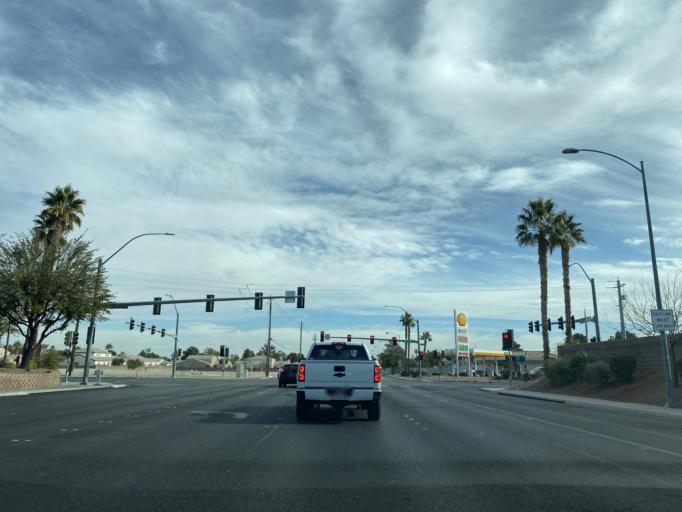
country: US
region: Nevada
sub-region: Clark County
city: Las Vegas
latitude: 36.2467
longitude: -115.2084
